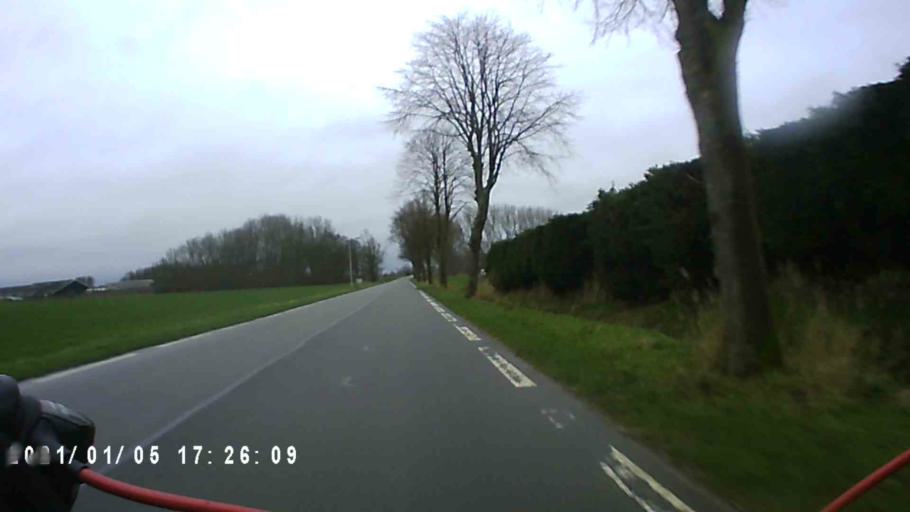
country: NL
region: Groningen
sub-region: Gemeente Delfzijl
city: Delfzijl
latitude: 53.2273
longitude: 6.9581
